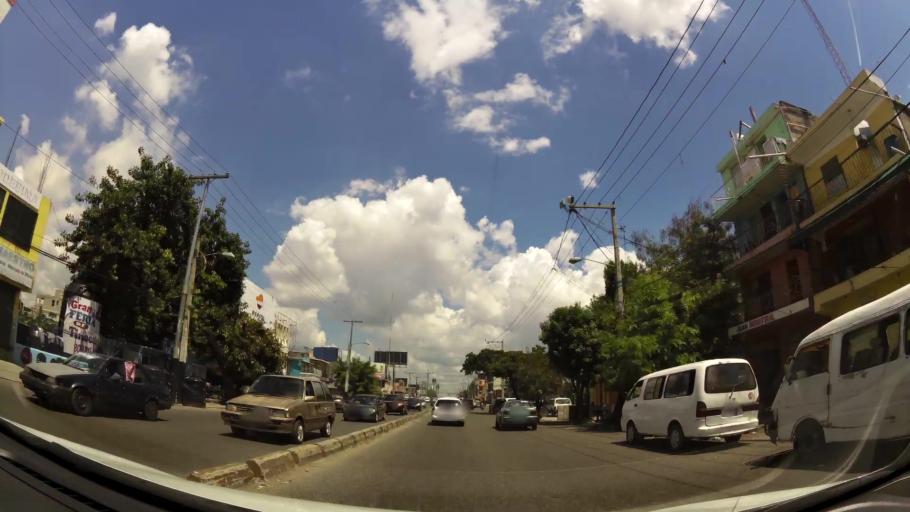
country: DO
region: Nacional
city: Ensanche Luperon
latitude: 18.5015
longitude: -69.8875
